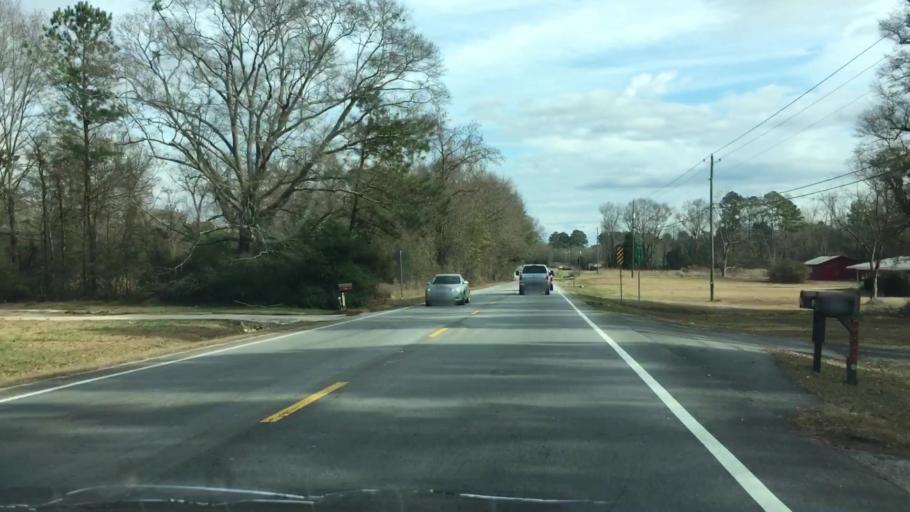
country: US
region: Georgia
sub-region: Henry County
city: McDonough
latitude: 33.4278
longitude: -84.0854
